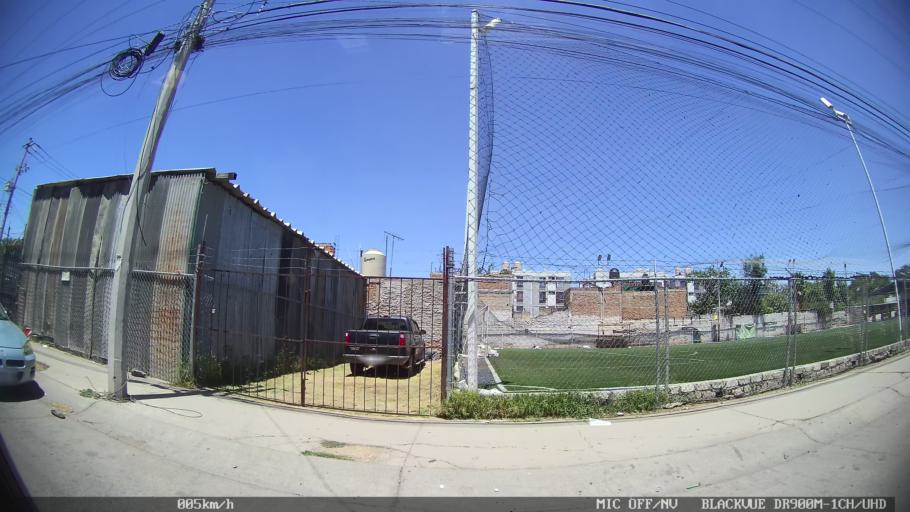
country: MX
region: Jalisco
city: Tlaquepaque
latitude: 20.6579
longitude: -103.2729
